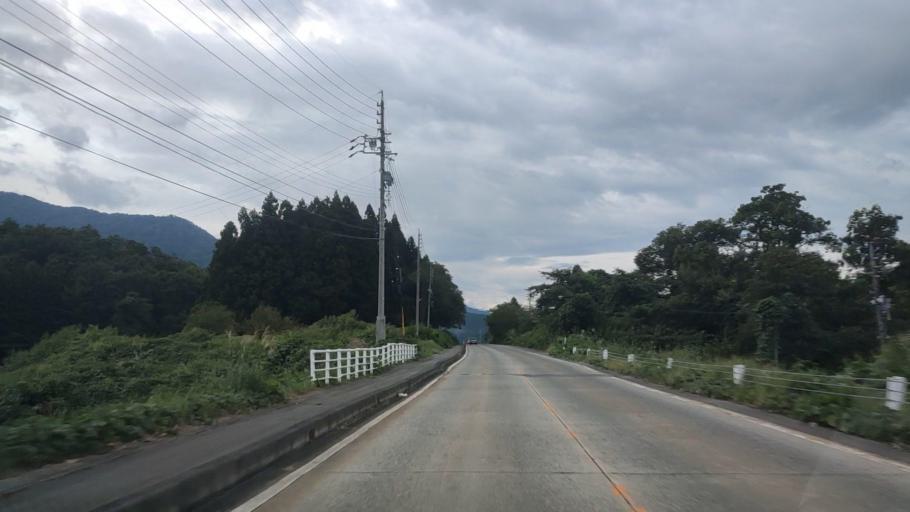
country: JP
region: Nagano
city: Iiyama
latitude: 36.8896
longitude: 138.4082
